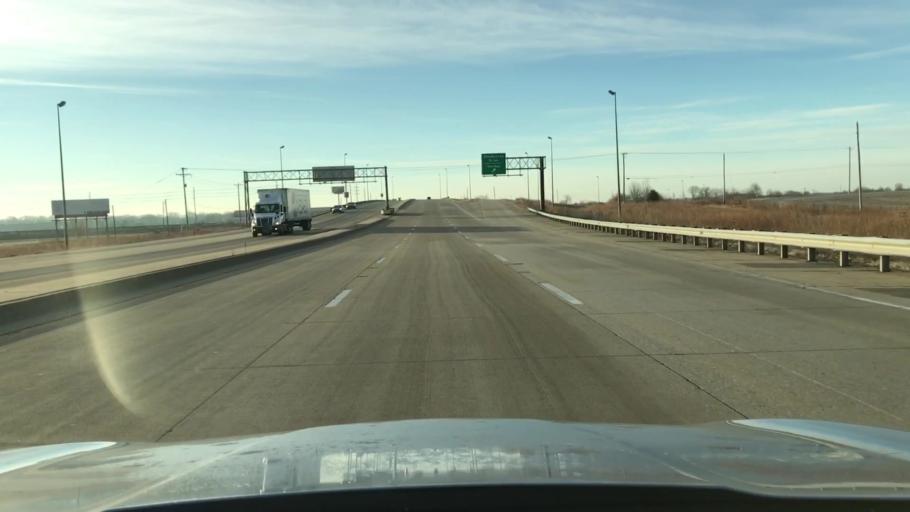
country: US
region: Illinois
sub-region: McLean County
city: Normal
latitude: 40.5339
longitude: -88.9514
